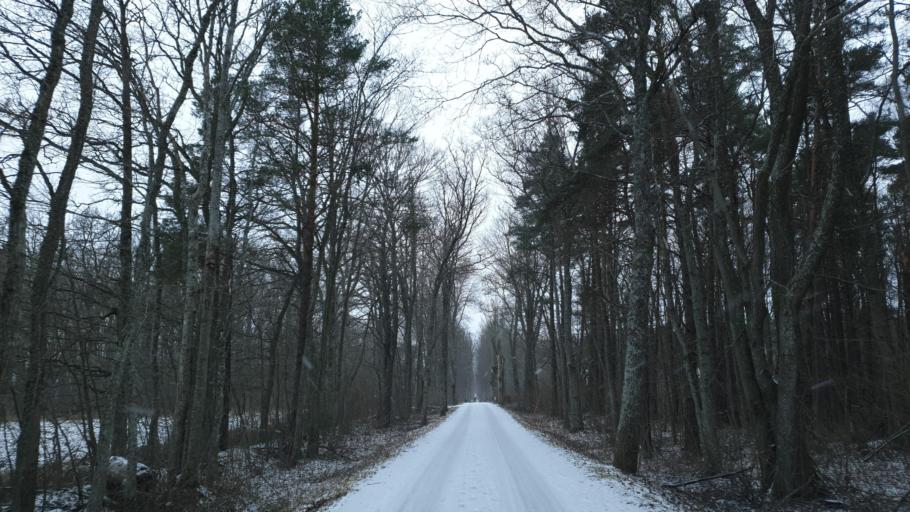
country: SE
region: Gotland
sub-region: Gotland
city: Visby
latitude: 57.5227
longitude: 18.4499
